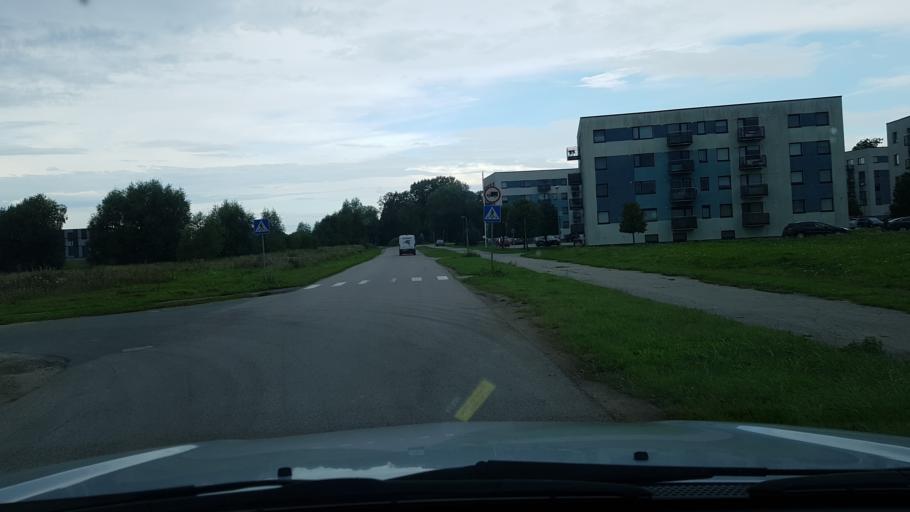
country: EE
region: Harju
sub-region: Rae vald
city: Jueri
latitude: 59.3521
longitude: 24.8925
